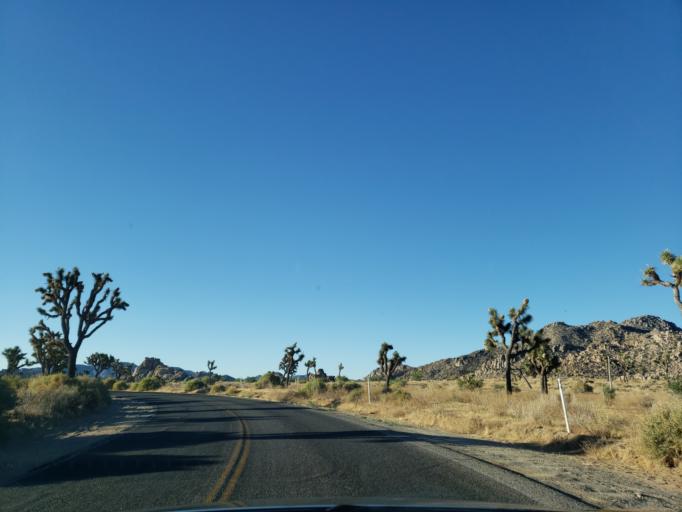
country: US
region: California
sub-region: San Bernardino County
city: Joshua Tree
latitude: 34.0459
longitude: -116.2008
